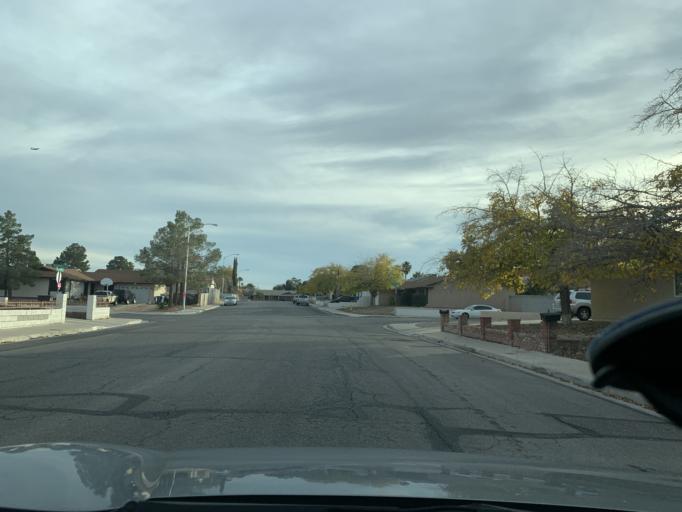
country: US
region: Nevada
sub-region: Clark County
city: Spring Valley
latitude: 36.0975
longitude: -115.2314
